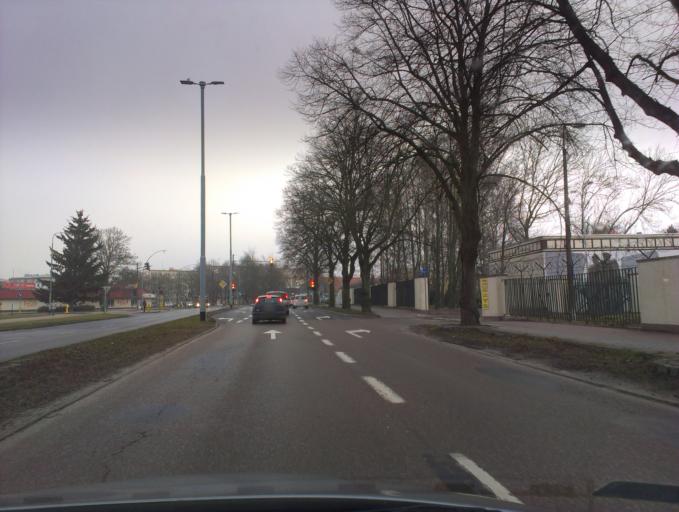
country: PL
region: West Pomeranian Voivodeship
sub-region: Koszalin
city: Koszalin
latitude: 54.1901
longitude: 16.2103
